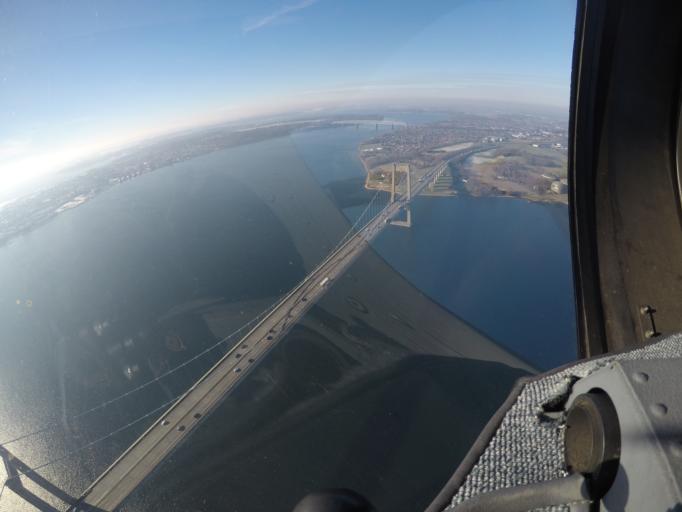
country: DK
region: South Denmark
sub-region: Middelfart Kommune
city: Strib
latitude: 55.5193
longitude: 9.7537
